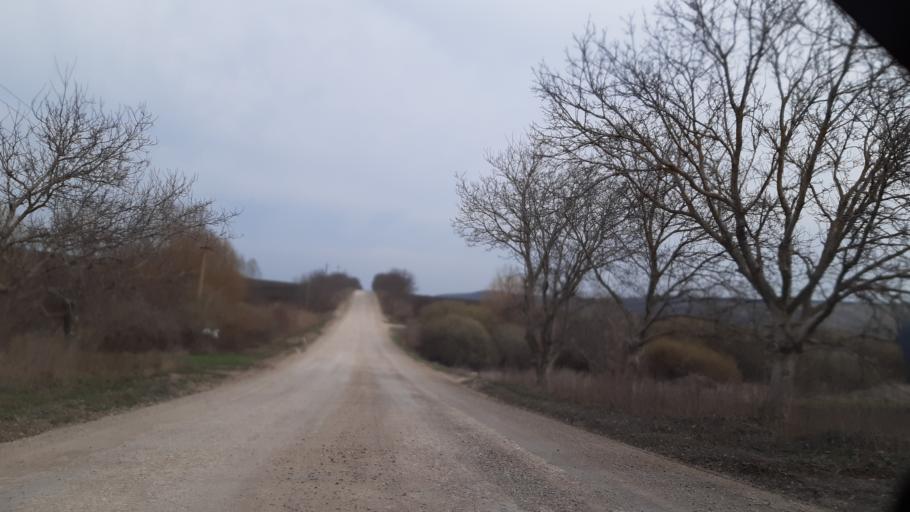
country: MD
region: Soldanesti
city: Soldanesti
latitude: 47.6977
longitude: 28.7280
